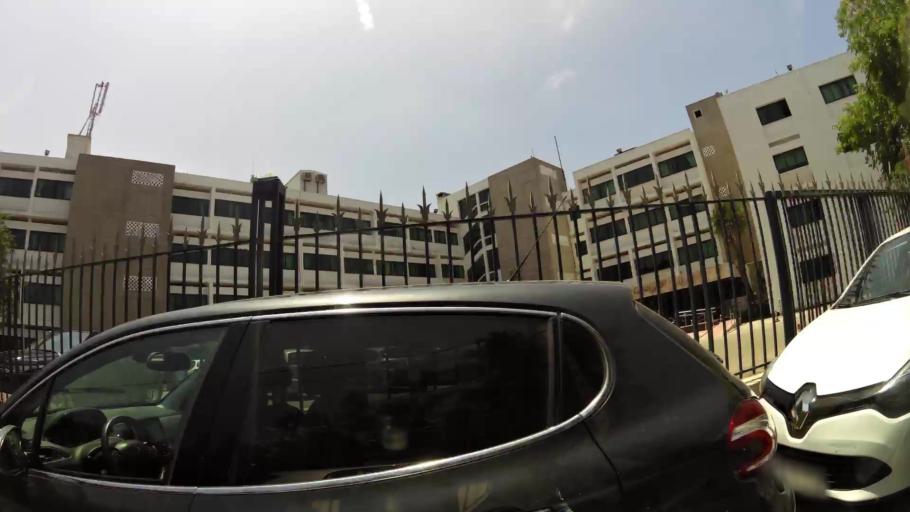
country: MA
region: Rabat-Sale-Zemmour-Zaer
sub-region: Rabat
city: Rabat
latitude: 34.0125
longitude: -6.8224
